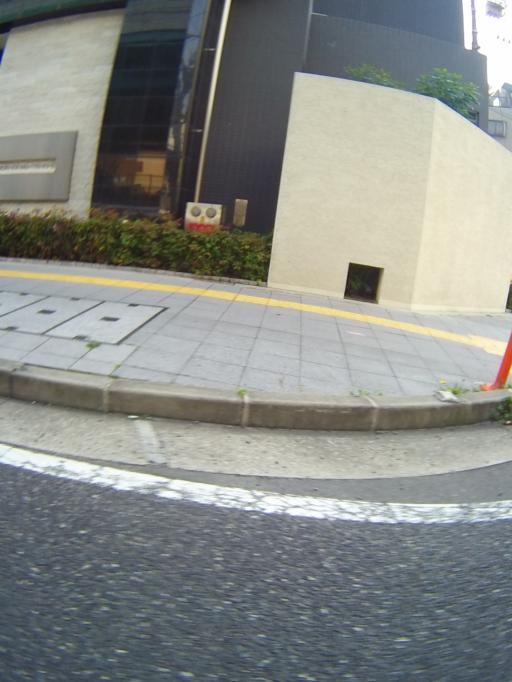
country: JP
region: Osaka
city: Osaka-shi
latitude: 34.6734
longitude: 135.4593
